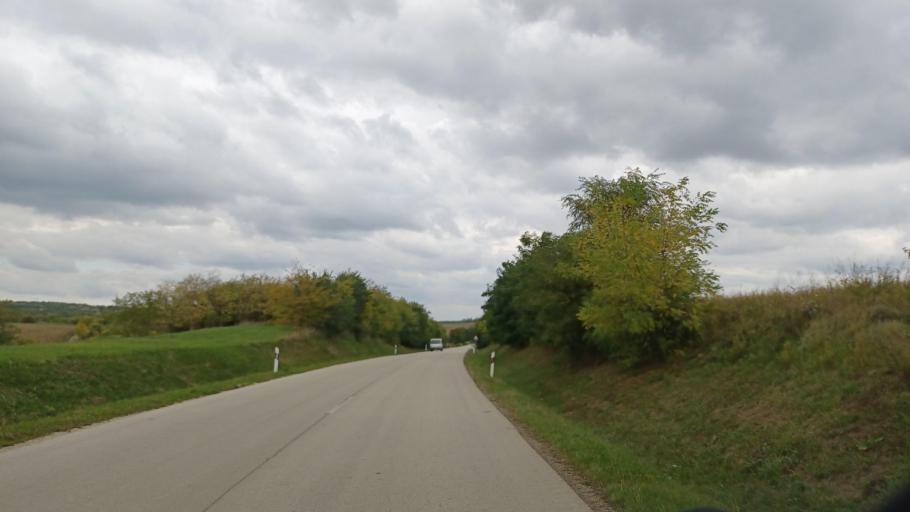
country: HU
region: Tolna
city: Simontornya
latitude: 46.7292
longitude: 18.5702
